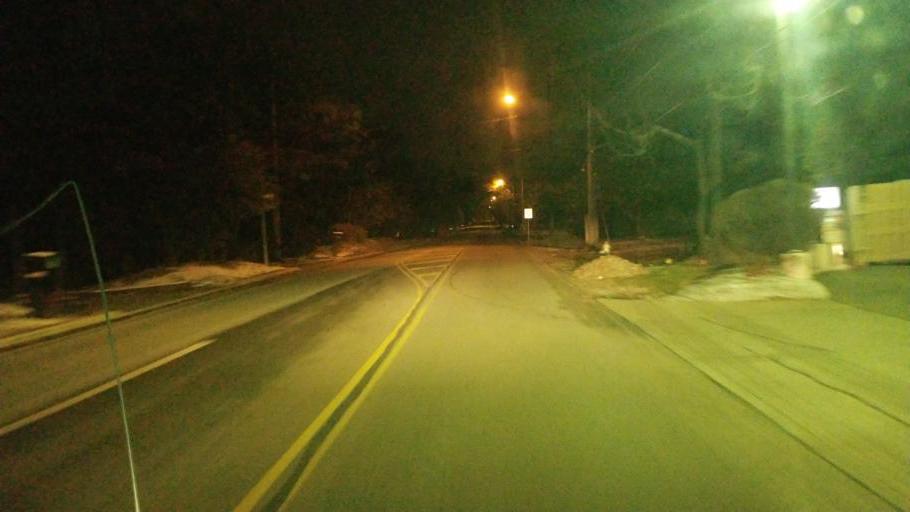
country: US
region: Ohio
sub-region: Cuyahoga County
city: Oakwood
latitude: 41.3579
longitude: -81.4985
